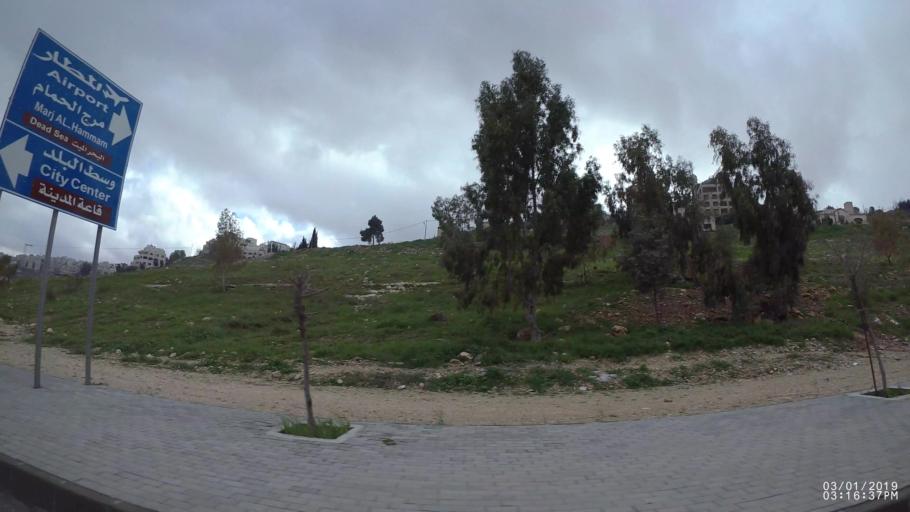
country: JO
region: Amman
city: Amman
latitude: 31.9464
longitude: 35.9050
